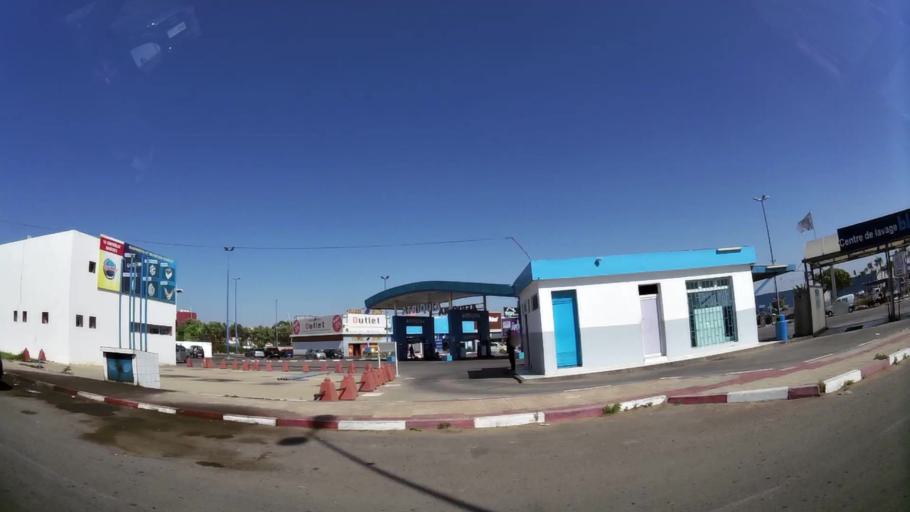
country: MA
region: Souss-Massa-Draa
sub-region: Agadir-Ida-ou-Tnan
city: Agadir
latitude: 30.3964
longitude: -9.5821
